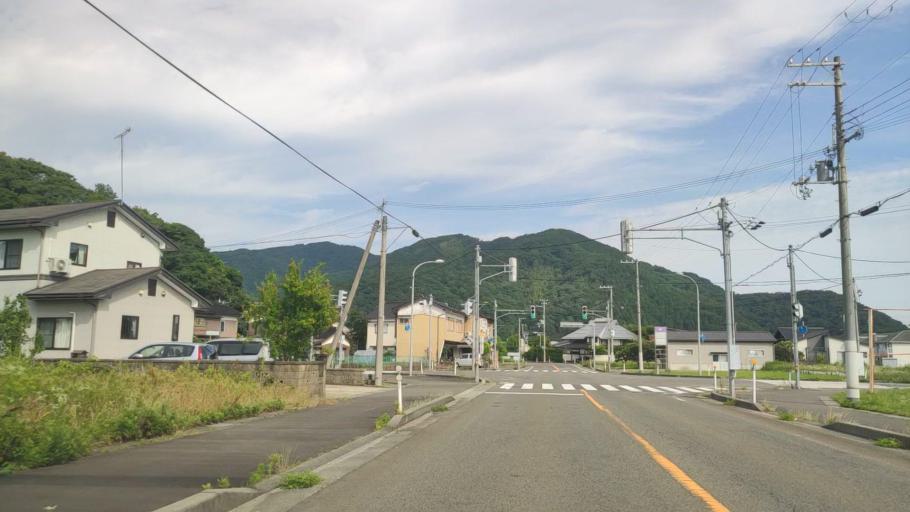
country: JP
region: Hyogo
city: Toyooka
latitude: 35.6422
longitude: 134.8333
